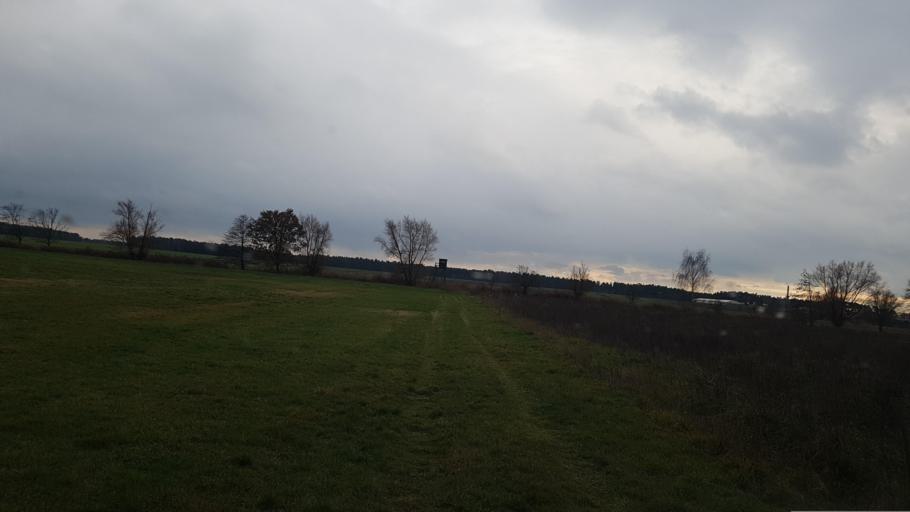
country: DE
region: Brandenburg
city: Ruckersdorf
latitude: 51.5606
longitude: 13.6078
